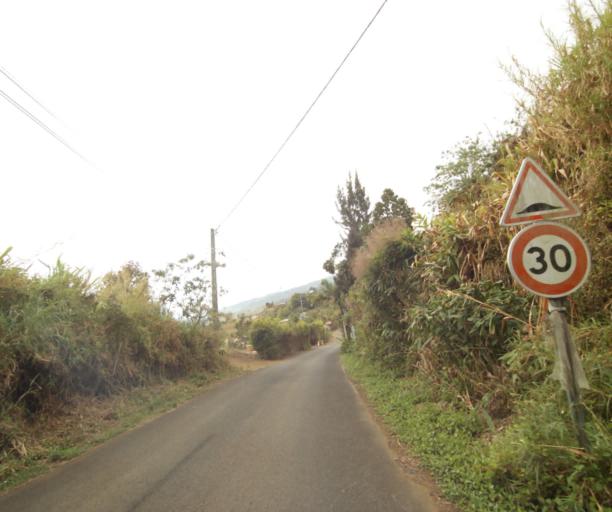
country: RE
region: Reunion
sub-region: Reunion
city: Saint-Paul
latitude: -21.0124
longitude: 55.3369
